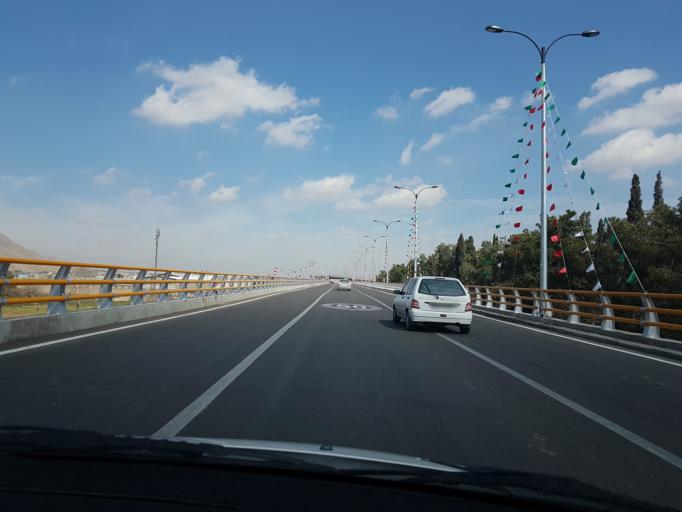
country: IR
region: Fars
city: Shiraz
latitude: 29.6121
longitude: 52.4681
